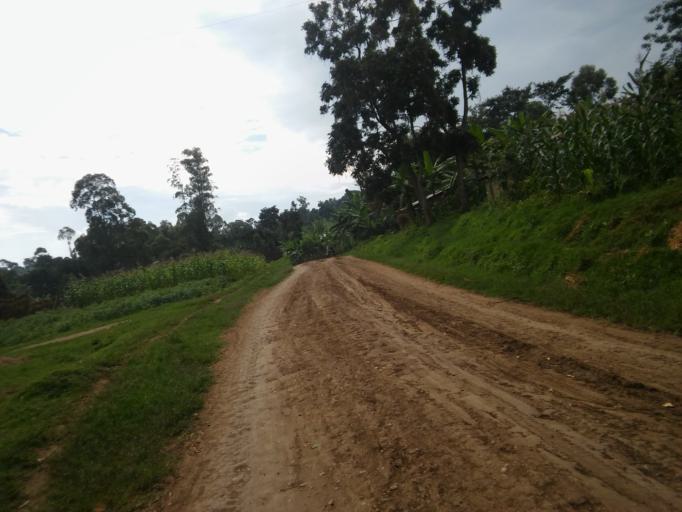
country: UG
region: Eastern Region
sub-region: Manafwa District
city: Manafwa
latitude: 0.8946
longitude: 34.3604
